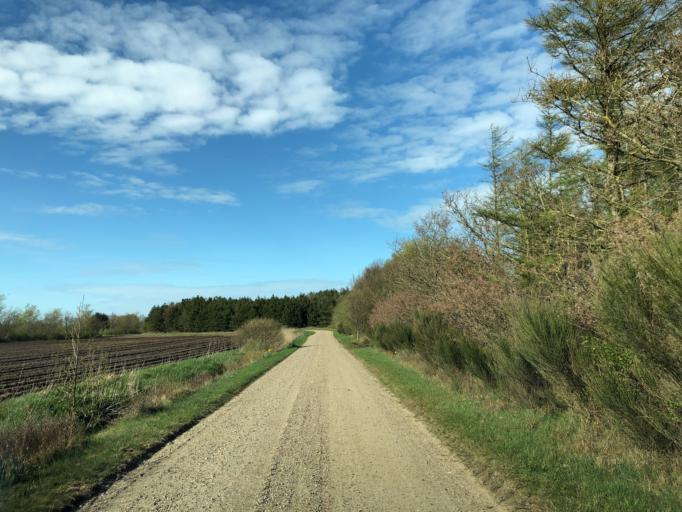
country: DK
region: Central Jutland
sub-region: Holstebro Kommune
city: Ulfborg
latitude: 56.2619
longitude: 8.3276
